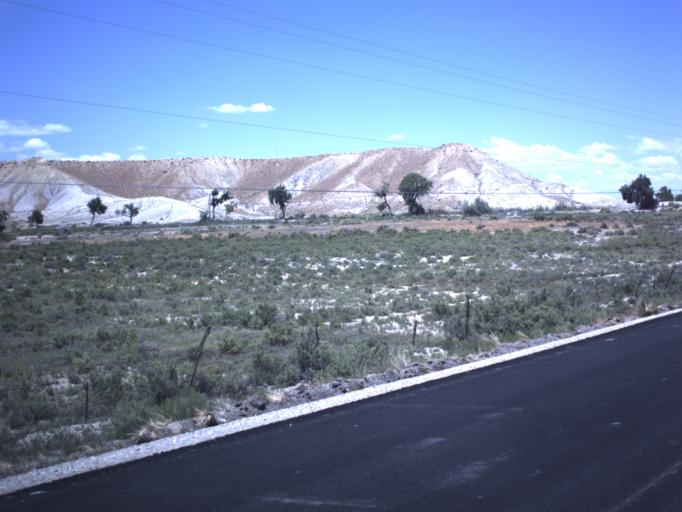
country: US
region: Utah
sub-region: Emery County
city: Castle Dale
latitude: 39.2325
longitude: -111.0136
